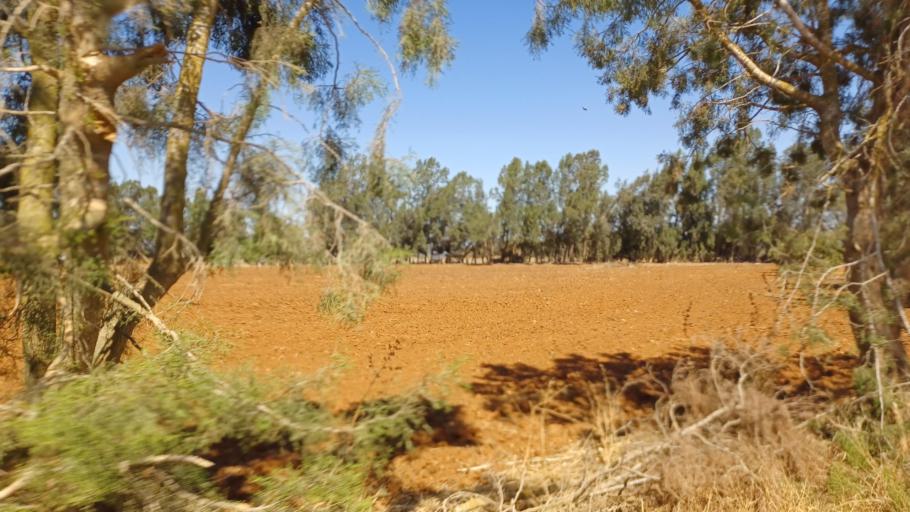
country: CY
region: Ammochostos
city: Avgorou
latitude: 35.0605
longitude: 33.8293
